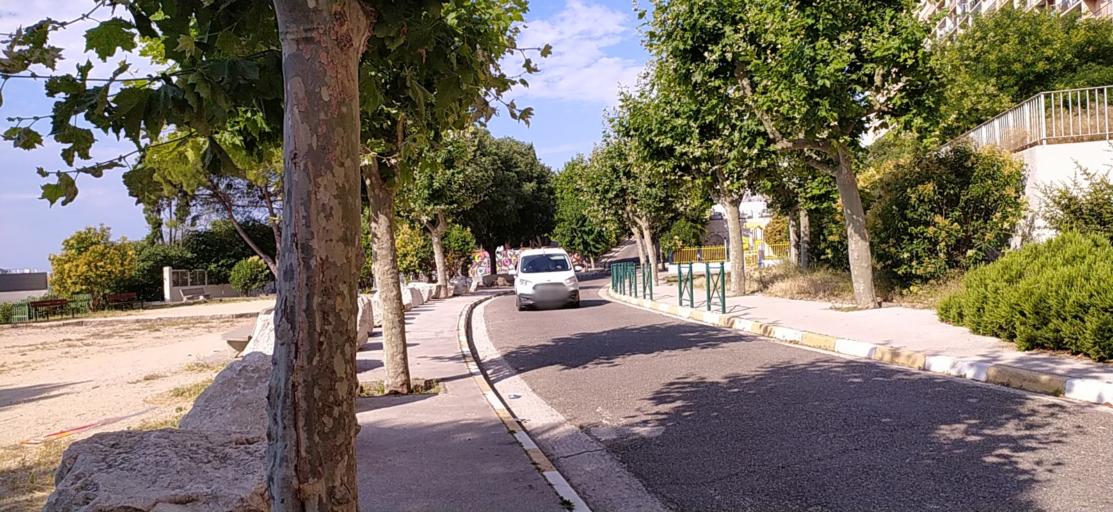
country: FR
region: Provence-Alpes-Cote d'Azur
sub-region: Departement des Bouches-du-Rhone
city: Marseille 14
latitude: 43.3435
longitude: 5.3562
